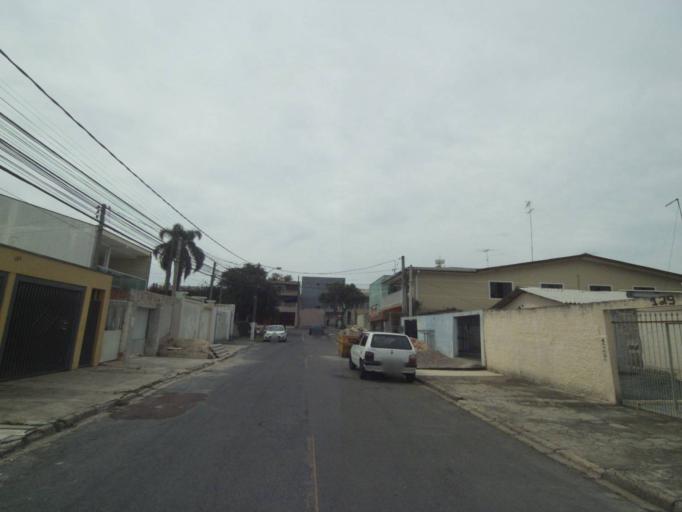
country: BR
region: Parana
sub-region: Curitiba
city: Curitiba
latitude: -25.5144
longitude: -49.3307
